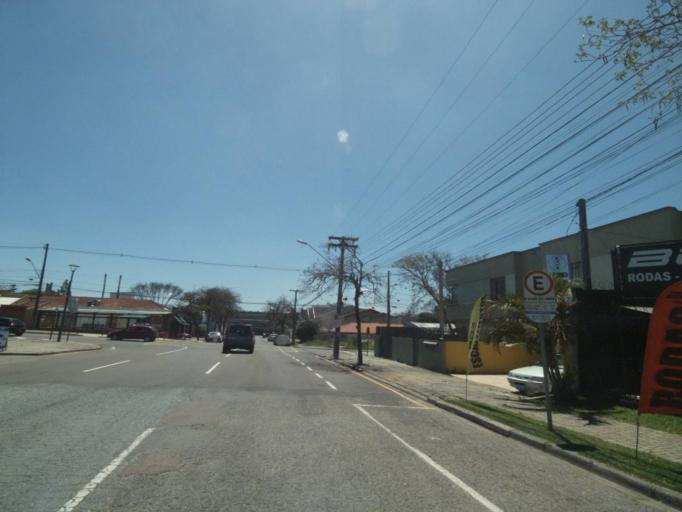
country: BR
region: Parana
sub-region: Curitiba
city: Curitiba
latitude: -25.3977
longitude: -49.2358
